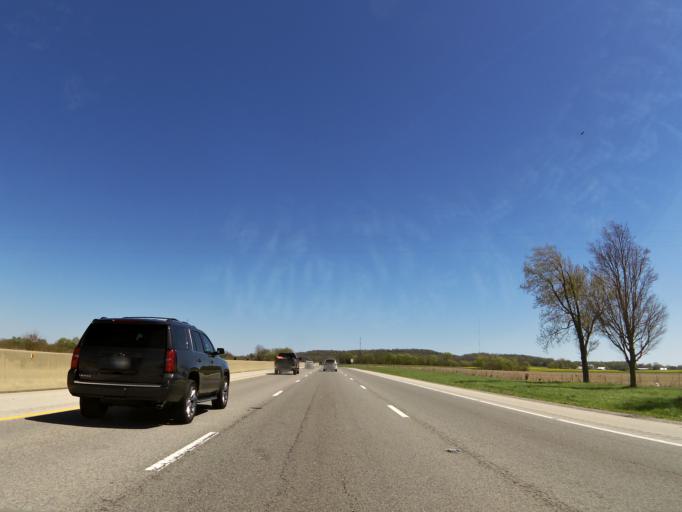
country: US
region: Kentucky
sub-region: Edmonson County
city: Brownsville
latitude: 37.0415
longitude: -86.1994
